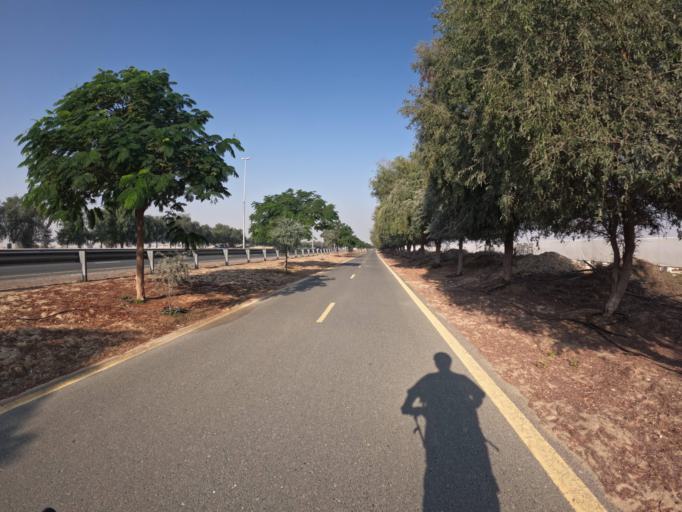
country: AE
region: Dubai
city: Dubai
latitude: 24.9913
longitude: 55.3181
